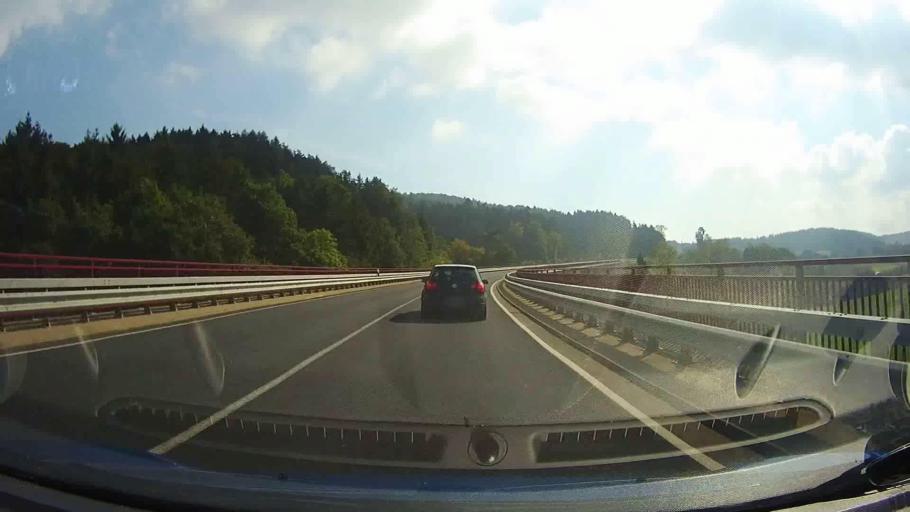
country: DE
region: Lower Saxony
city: Hardegsen
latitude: 51.6552
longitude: 9.7640
